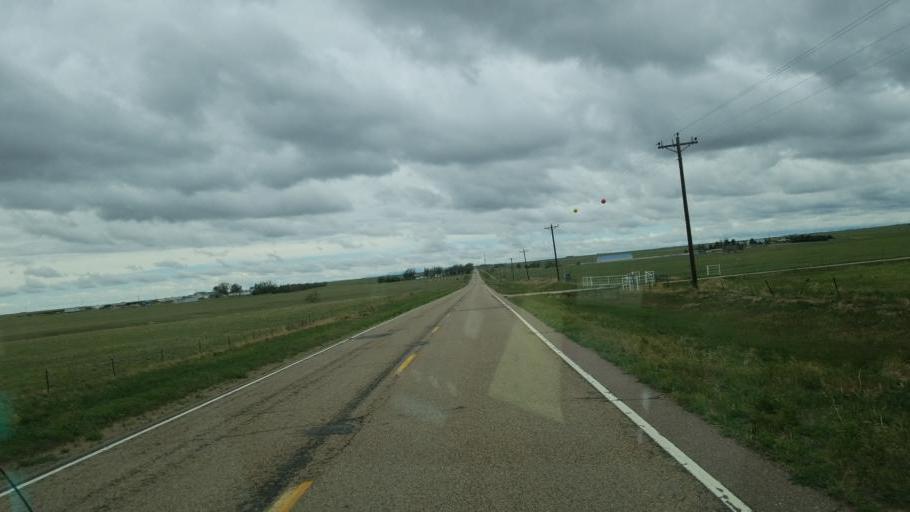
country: US
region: Colorado
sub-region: El Paso County
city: Ellicott
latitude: 38.8397
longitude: -103.9882
